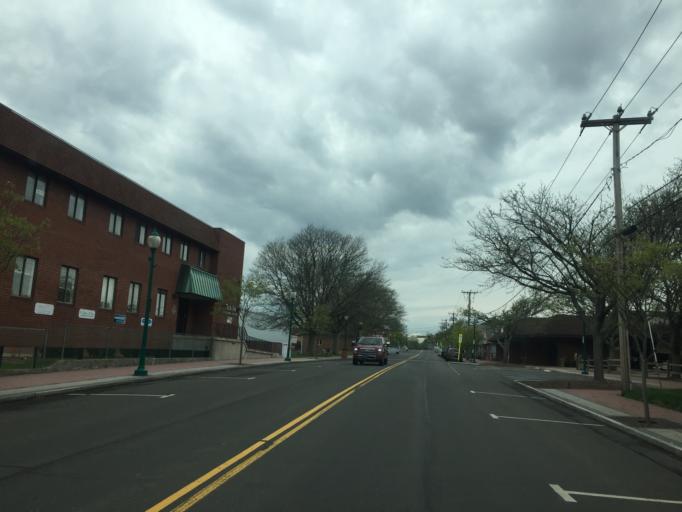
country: US
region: Connecticut
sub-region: Hartford County
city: Newington
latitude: 41.6968
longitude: -72.7192
